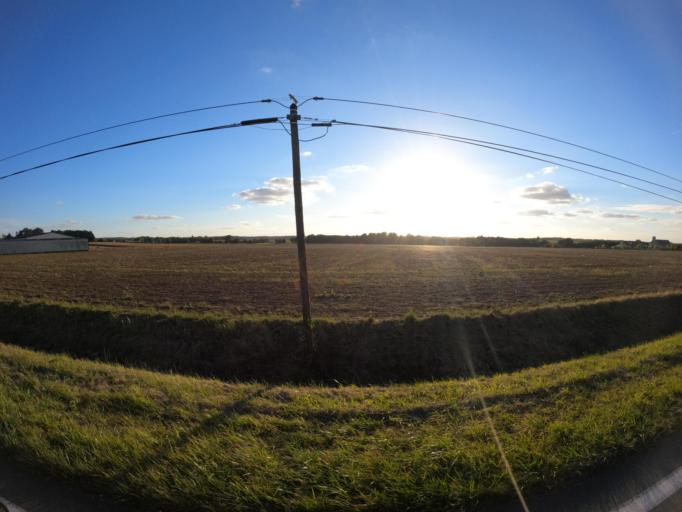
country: FR
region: Pays de la Loire
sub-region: Departement de Maine-et-Loire
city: Brissac-Quince
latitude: 47.3238
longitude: -0.4143
